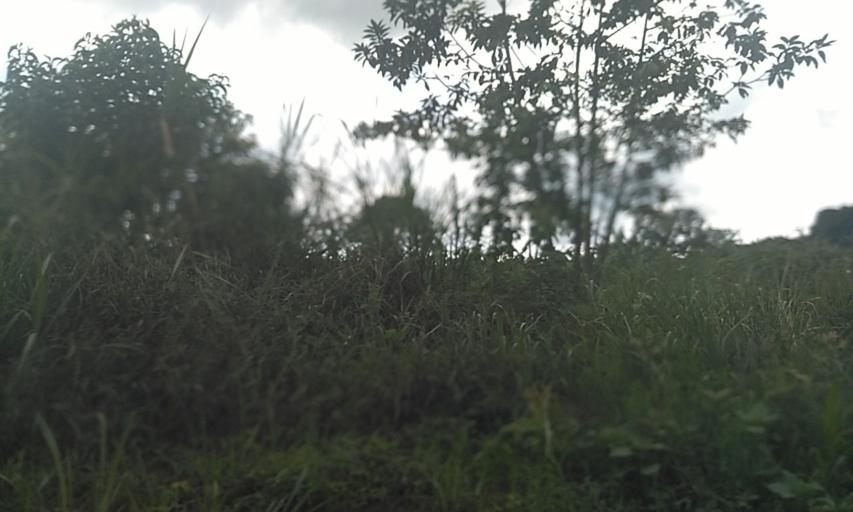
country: UG
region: Central Region
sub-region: Wakiso District
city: Wakiso
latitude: 0.3560
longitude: 32.4585
